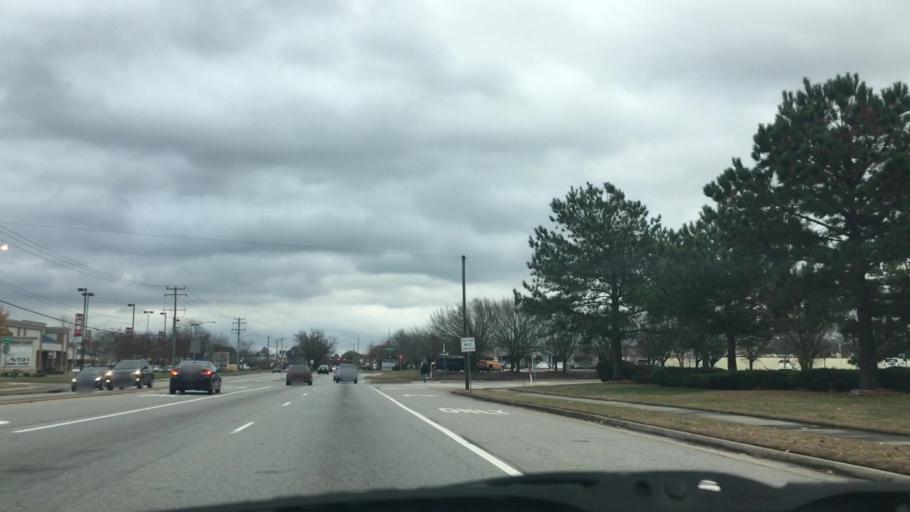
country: US
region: Virginia
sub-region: City of Chesapeake
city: Chesapeake
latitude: 36.8226
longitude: -76.1253
